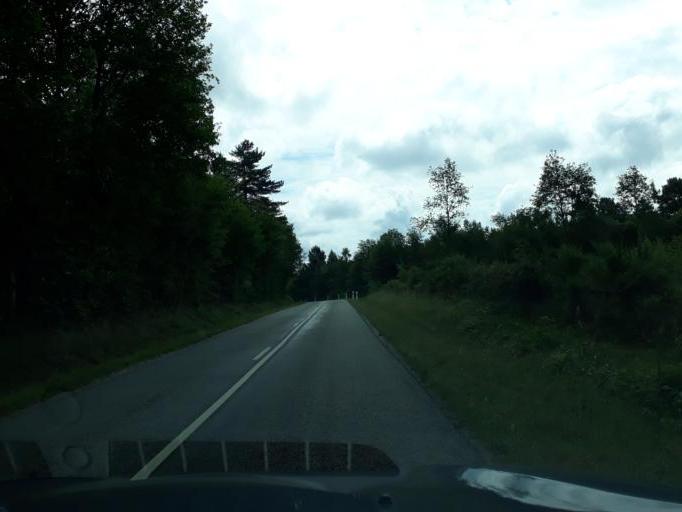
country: FR
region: Centre
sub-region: Departement du Loir-et-Cher
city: Chaumont-sur-Tharonne
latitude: 47.6274
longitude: 1.8643
